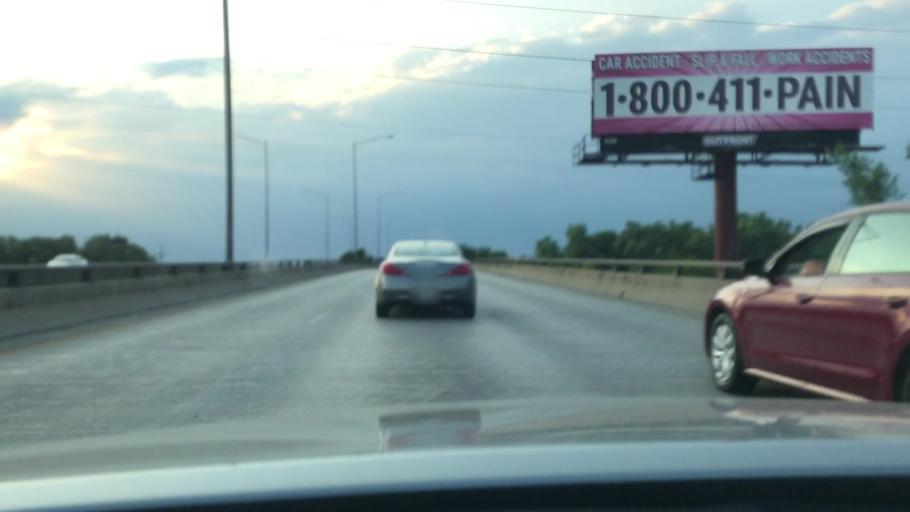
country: US
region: Illinois
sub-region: Cook County
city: Willow Springs
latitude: 41.7481
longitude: -87.8555
